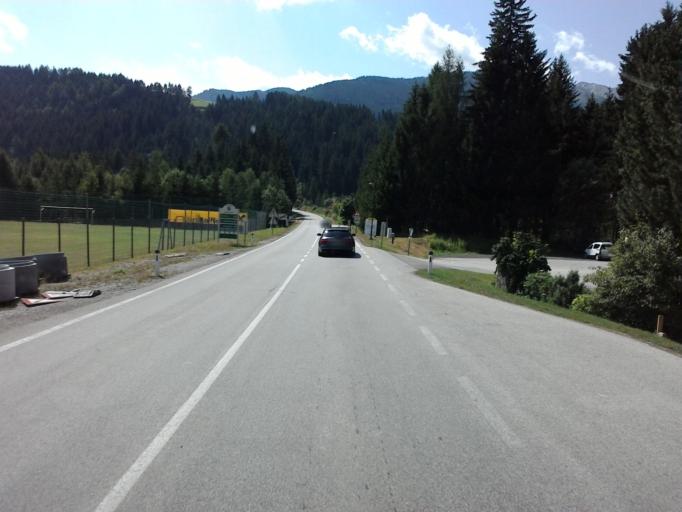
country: AT
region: Tyrol
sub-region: Politischer Bezirk Lienz
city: Heinfels
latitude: 46.7467
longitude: 12.4662
